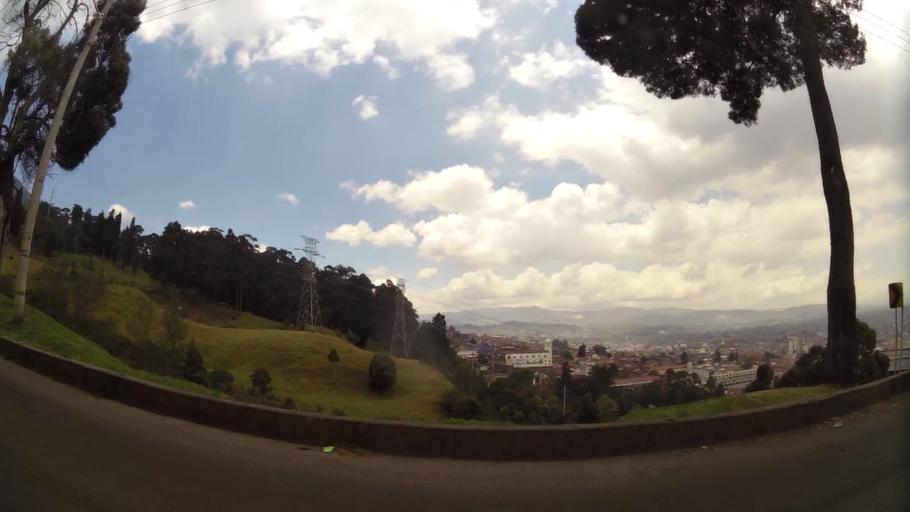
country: CO
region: Bogota D.C.
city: Bogota
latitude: 4.5963
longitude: -74.0663
